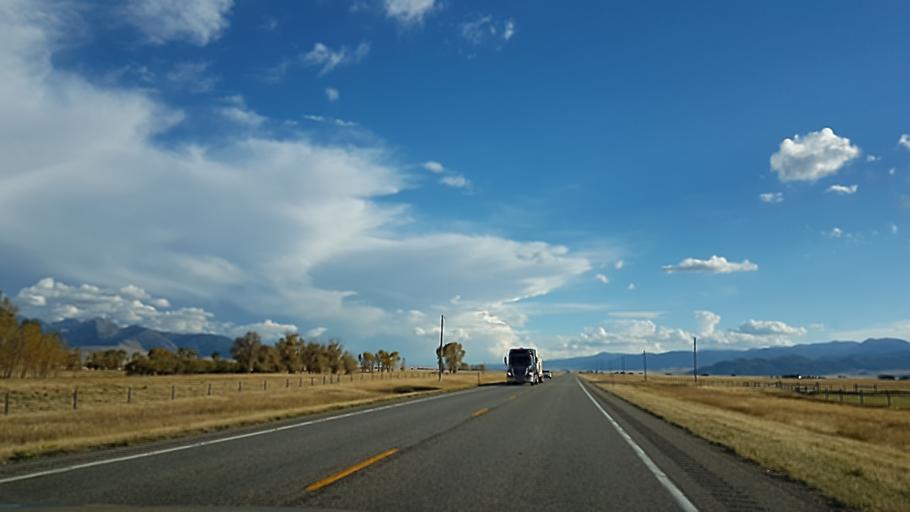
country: US
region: Montana
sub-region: Madison County
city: Virginia City
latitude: 45.1972
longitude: -111.6788
